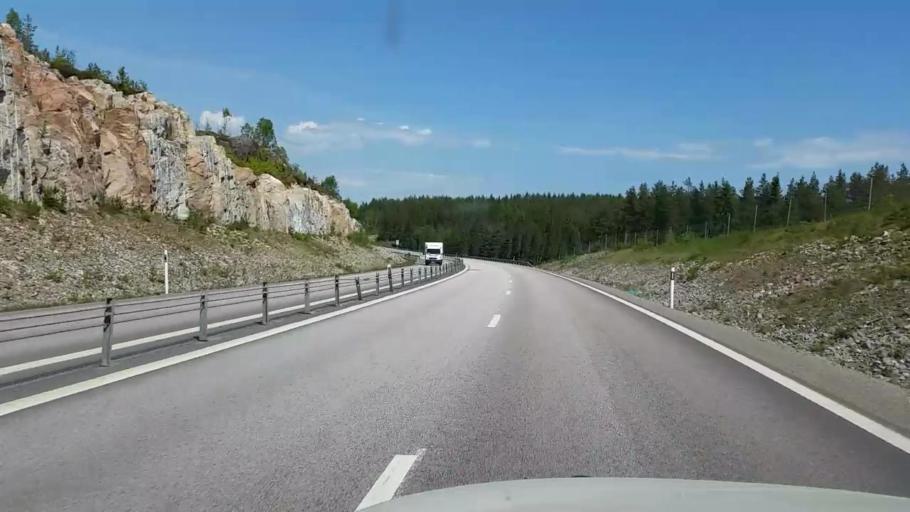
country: SE
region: Gaevleborg
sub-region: Hudiksvalls Kommun
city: Hudiksvall
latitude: 61.7242
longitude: 17.0637
